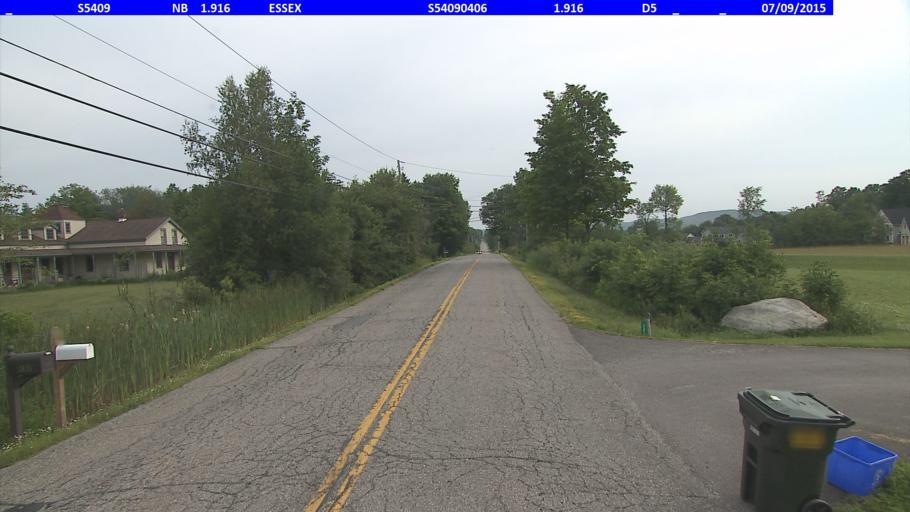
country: US
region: Vermont
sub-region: Chittenden County
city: Essex Junction
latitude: 44.5366
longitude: -73.0746
